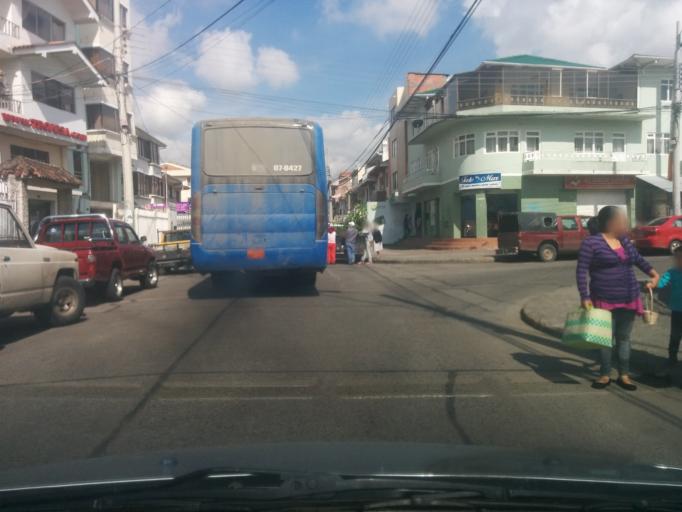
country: EC
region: Azuay
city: Cuenca
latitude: -2.9019
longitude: -78.9926
